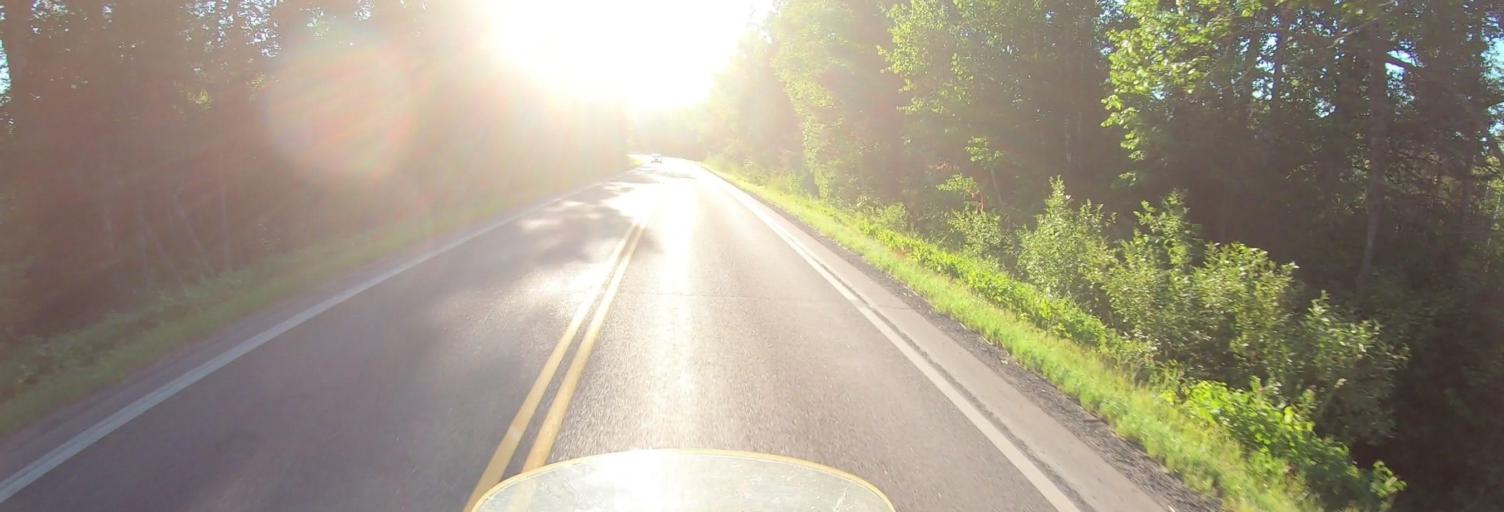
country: US
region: Minnesota
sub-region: Saint Louis County
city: Ely
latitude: 47.9317
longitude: -91.7125
